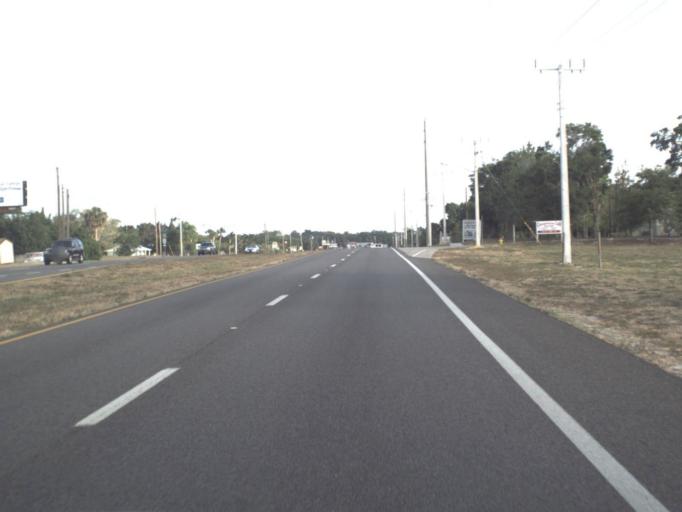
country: US
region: Florida
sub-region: Brevard County
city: Sharpes
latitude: 28.4217
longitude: -80.7571
